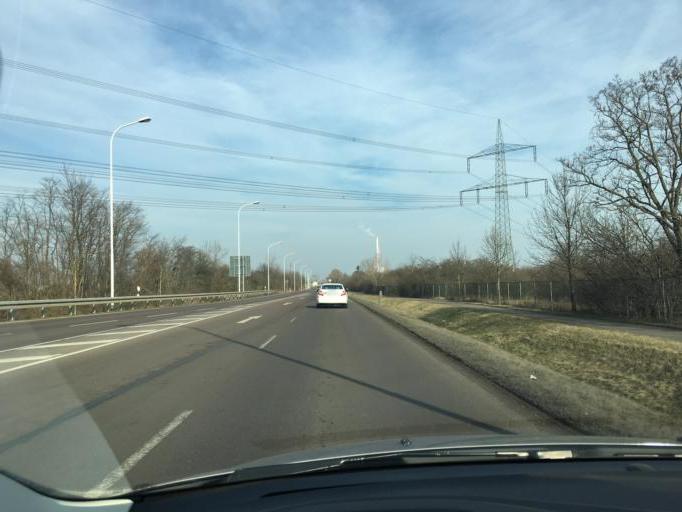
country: DE
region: Saxony-Anhalt
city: Schkopau
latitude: 51.4412
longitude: 11.9890
